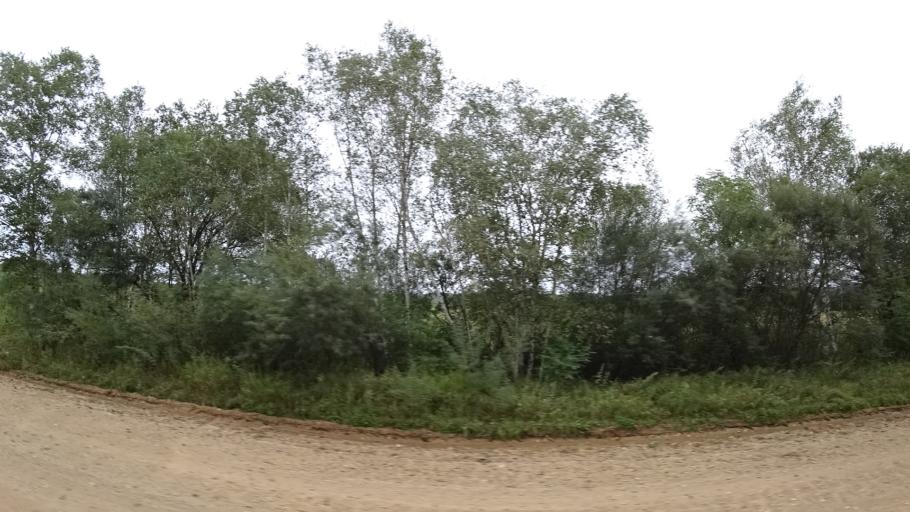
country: RU
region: Primorskiy
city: Rettikhovka
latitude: 44.1496
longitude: 132.6777
